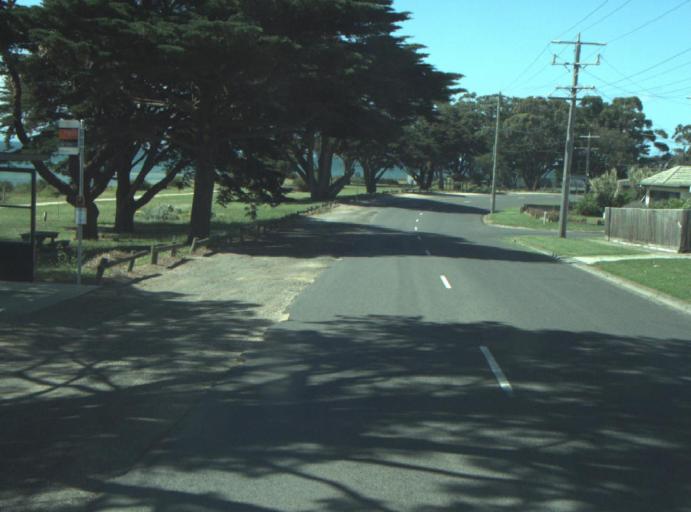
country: AU
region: Victoria
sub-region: Queenscliffe
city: Queenscliff
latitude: -38.1714
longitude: 144.7186
